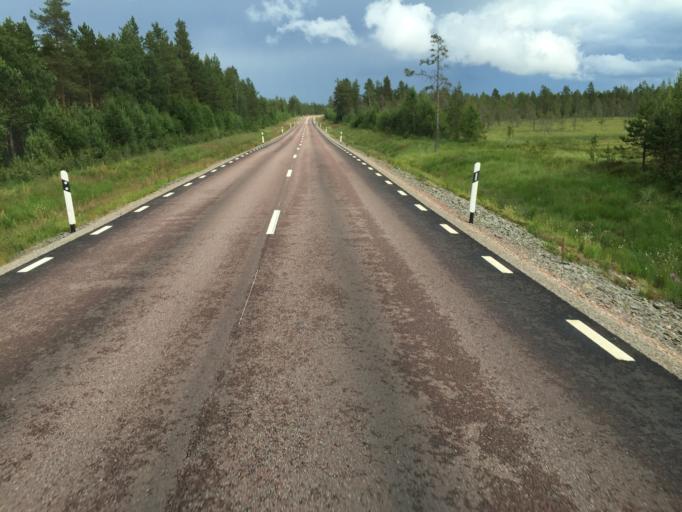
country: SE
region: Dalarna
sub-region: Vansbro Kommun
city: Vansbro
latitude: 60.8251
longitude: 14.0527
